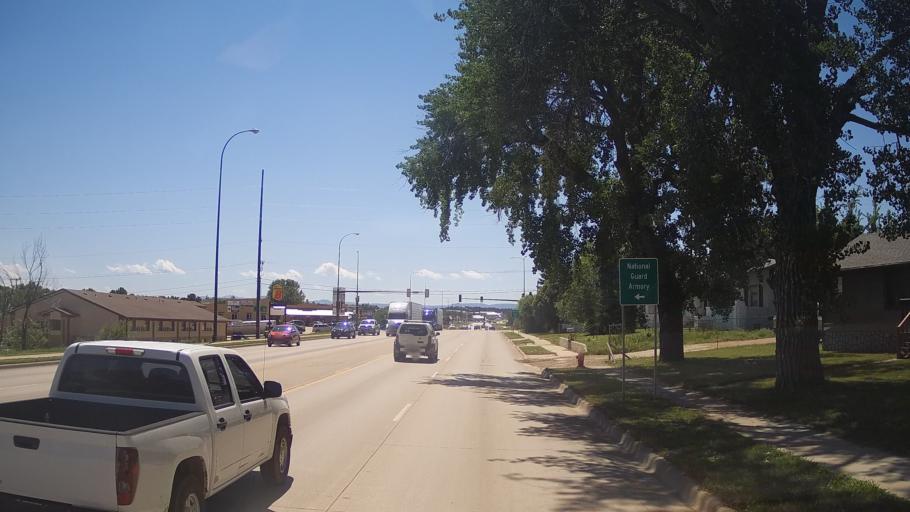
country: US
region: South Dakota
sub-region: Butte County
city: Belle Fourche
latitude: 44.6640
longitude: -103.8540
